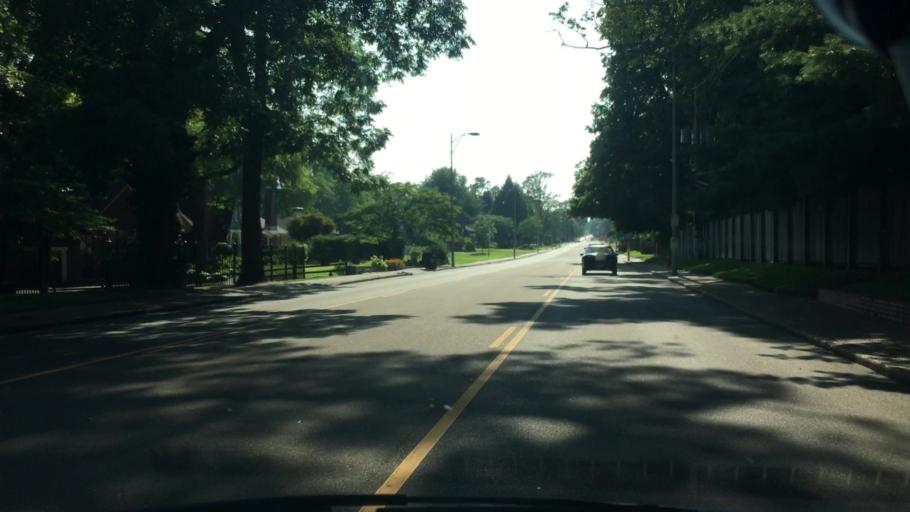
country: US
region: Indiana
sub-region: Vanderburgh County
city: Evansville
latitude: 37.9699
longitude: -87.5221
